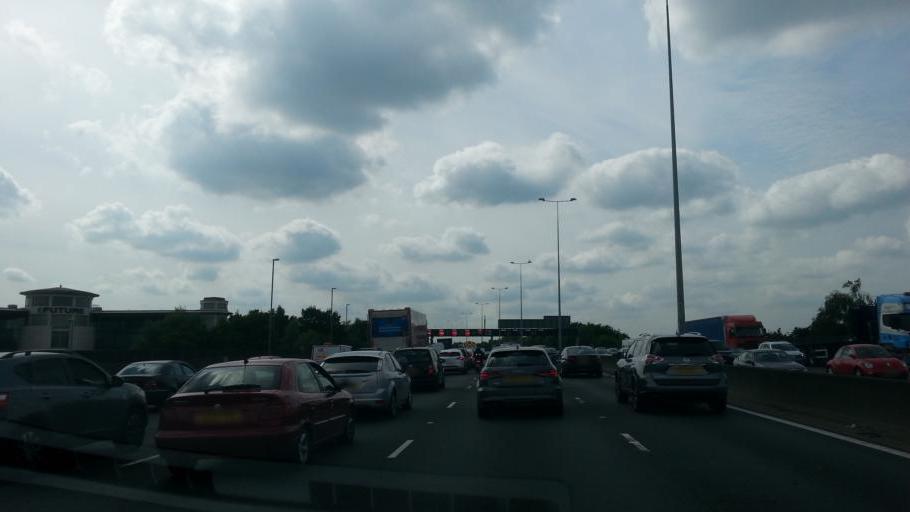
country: GB
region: England
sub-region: Surrey
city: Egham
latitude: 51.4360
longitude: -0.5363
